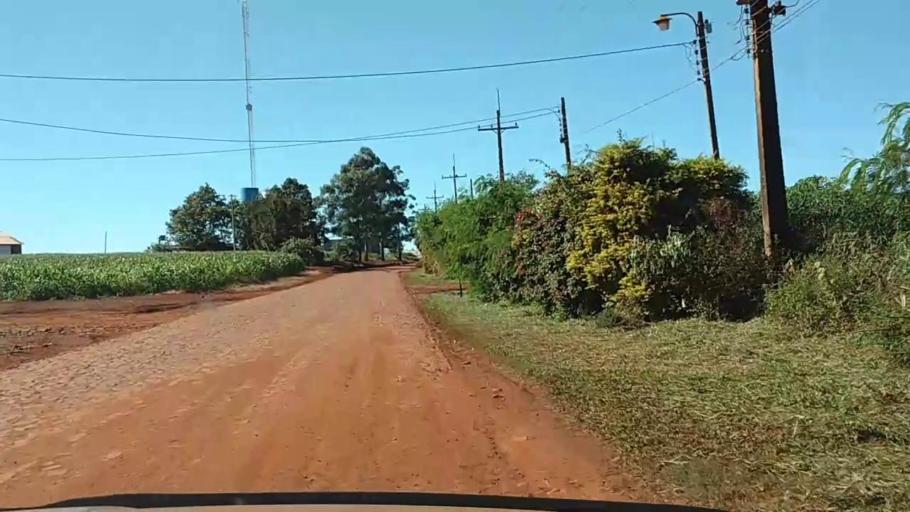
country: PY
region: Alto Parana
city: Naranjal
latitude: -25.8960
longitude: -55.4601
